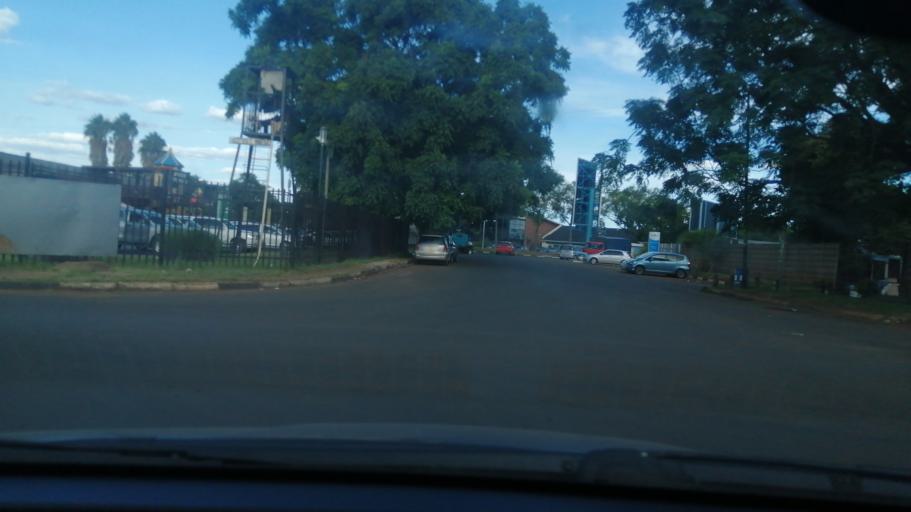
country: ZW
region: Harare
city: Harare
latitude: -17.7611
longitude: 31.0855
